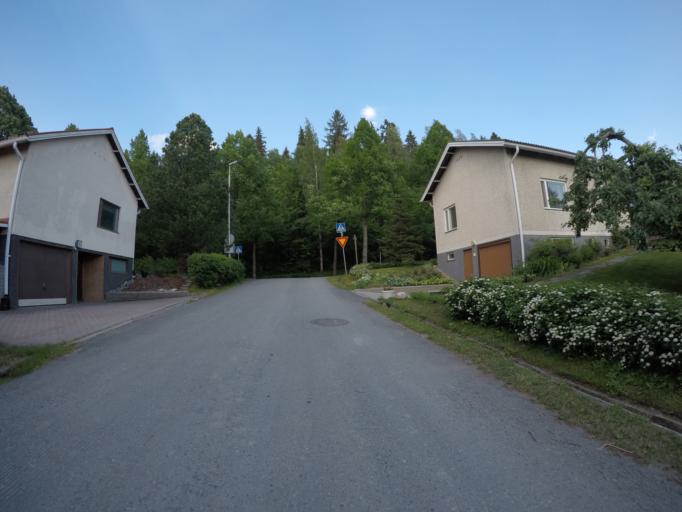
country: FI
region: Haeme
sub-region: Haemeenlinna
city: Haemeenlinna
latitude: 61.0149
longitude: 24.4538
